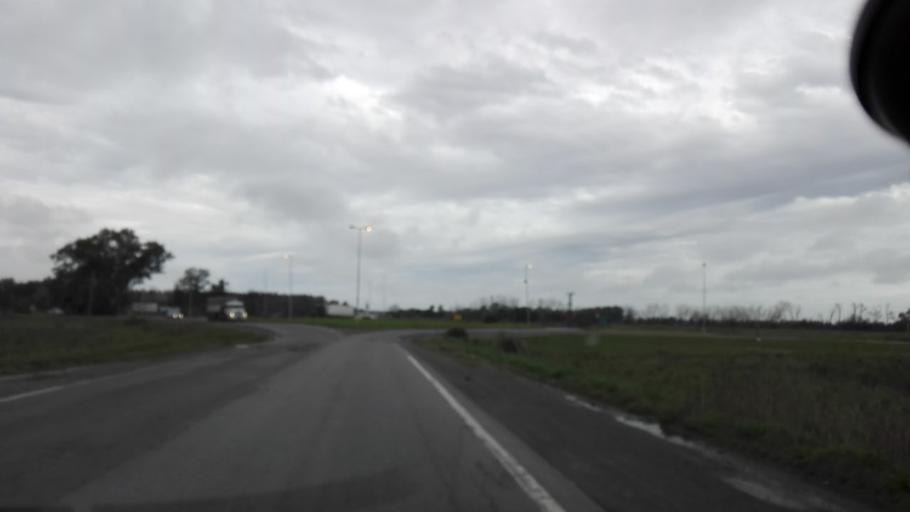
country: AR
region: Buenos Aires
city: San Miguel del Monte
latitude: -35.4375
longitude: -58.7814
